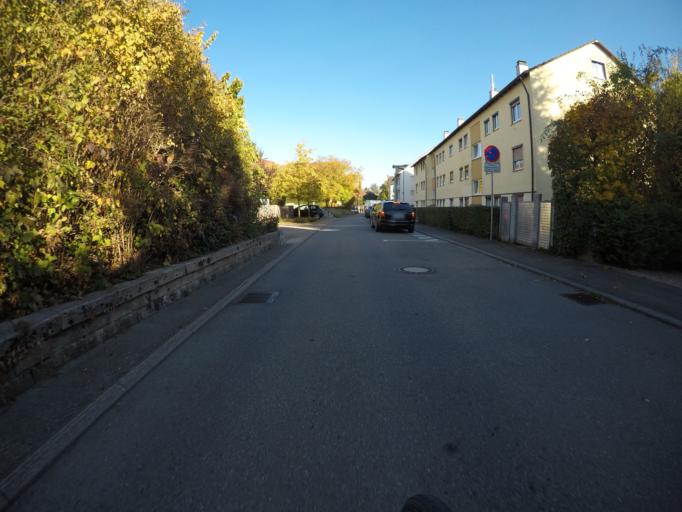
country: DE
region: Baden-Wuerttemberg
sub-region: Regierungsbezirk Stuttgart
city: Herrenberg
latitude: 48.5970
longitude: 8.8595
